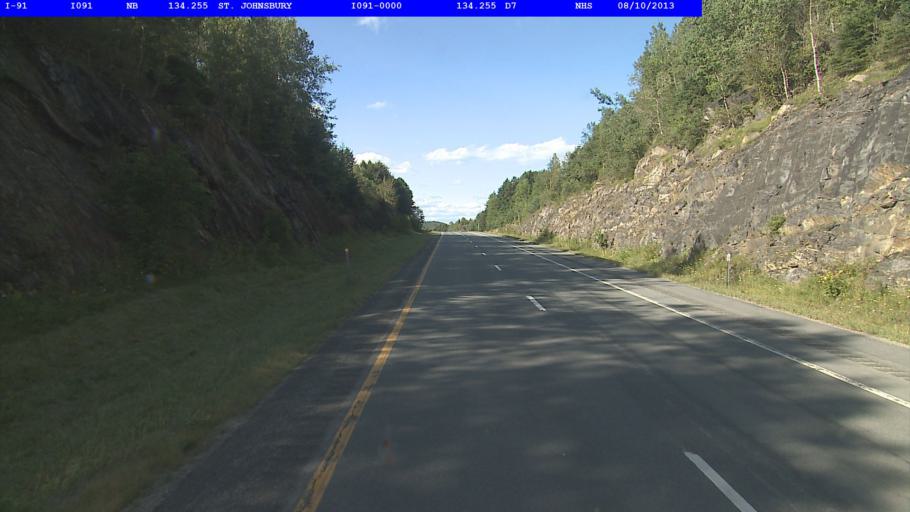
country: US
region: Vermont
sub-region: Caledonia County
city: Lyndon
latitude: 44.4781
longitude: -72.0231
